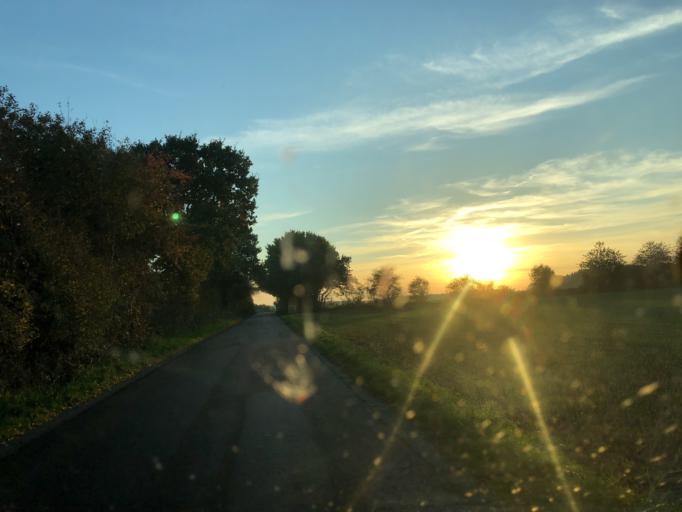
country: DK
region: South Denmark
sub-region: Vejle Kommune
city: Borkop
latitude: 55.6174
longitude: 9.6450
